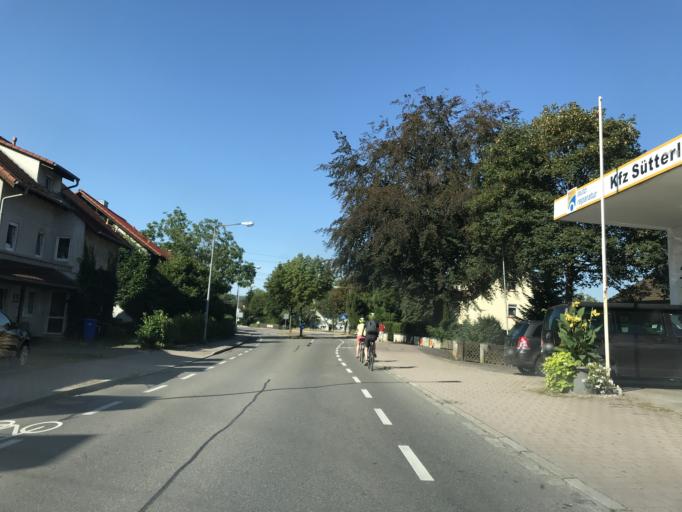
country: DE
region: Baden-Wuerttemberg
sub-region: Freiburg Region
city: Loerrach
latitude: 47.6306
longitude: 7.6850
